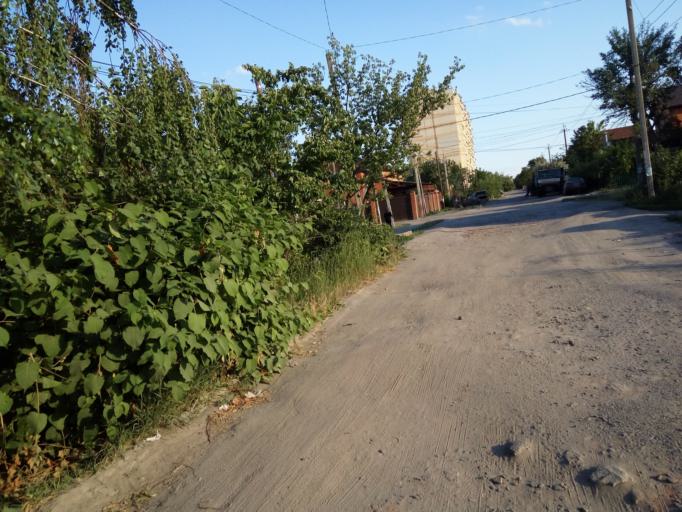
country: RU
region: Rostov
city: Bataysk
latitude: 47.1194
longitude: 39.7356
